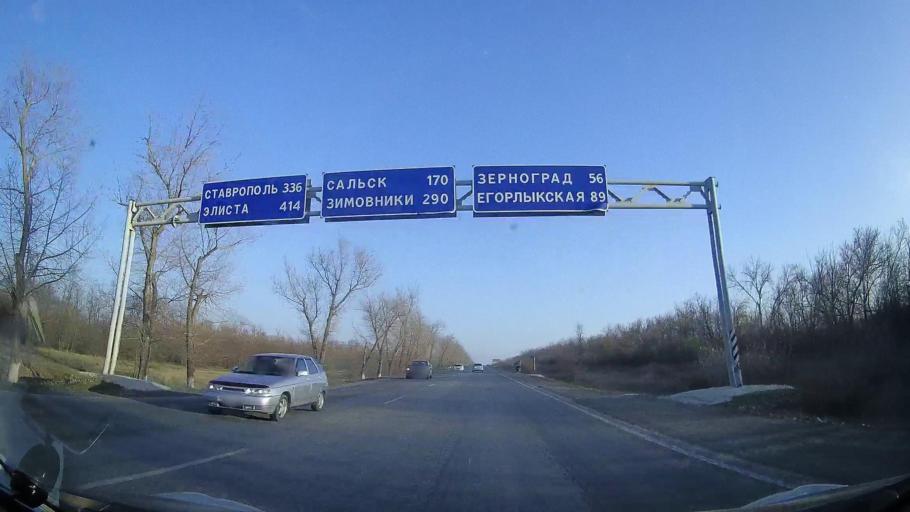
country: RU
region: Rostov
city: Bataysk
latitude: 47.0789
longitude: 39.7786
